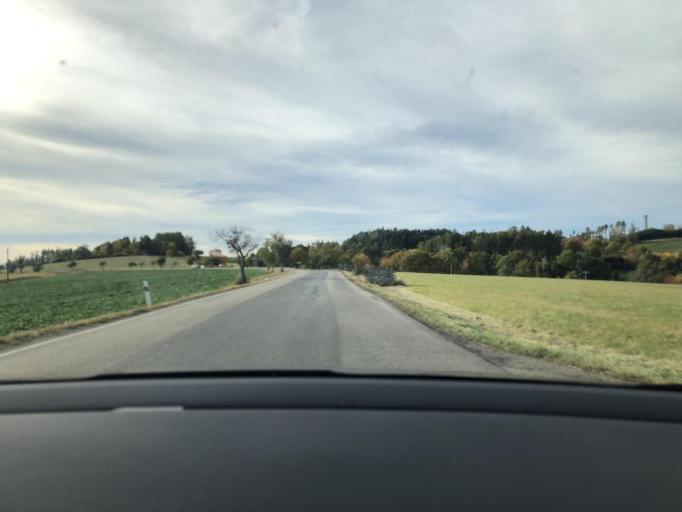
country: CZ
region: Central Bohemia
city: Divisov
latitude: 49.7872
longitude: 14.8378
